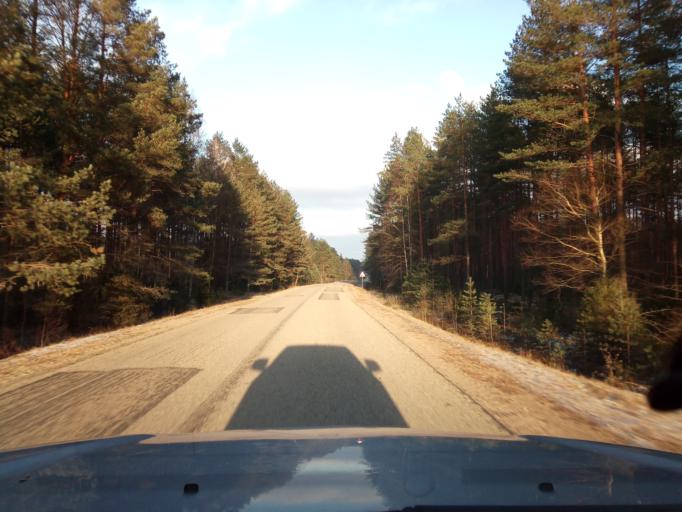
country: LT
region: Alytaus apskritis
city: Varena
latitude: 54.1243
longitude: 24.4541
